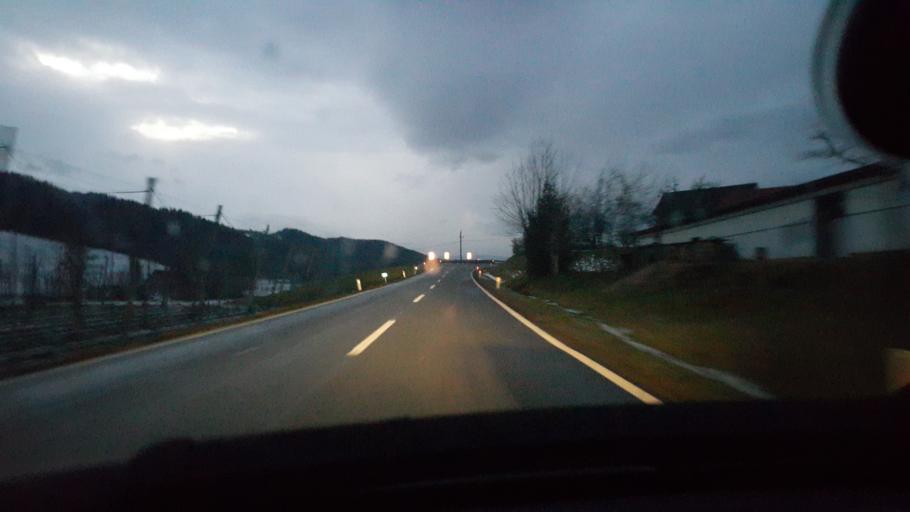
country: AT
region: Styria
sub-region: Politischer Bezirk Leibnitz
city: Leutschach
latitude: 46.6701
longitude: 15.4362
